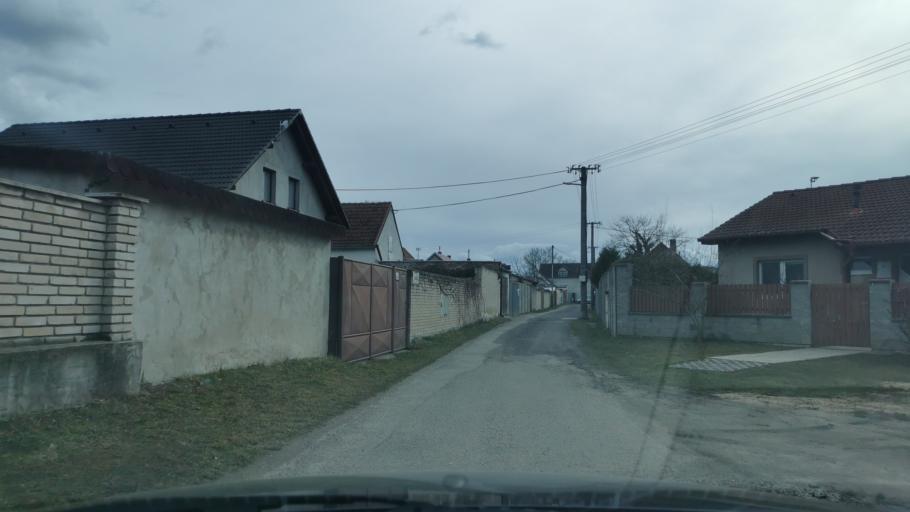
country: CZ
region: South Moravian
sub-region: Okres Breclav
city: Lanzhot
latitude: 48.6926
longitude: 17.0136
